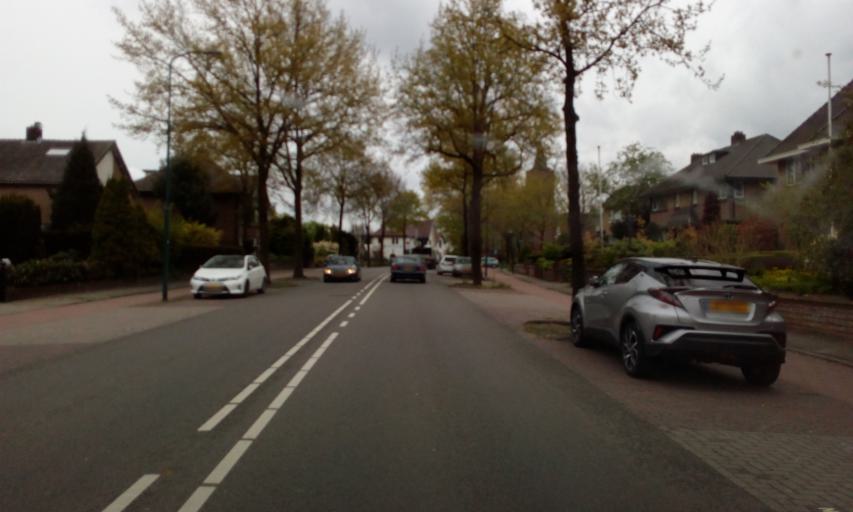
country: NL
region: Utrecht
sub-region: Gemeente Soest
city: Soest
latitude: 52.1755
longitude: 5.3099
